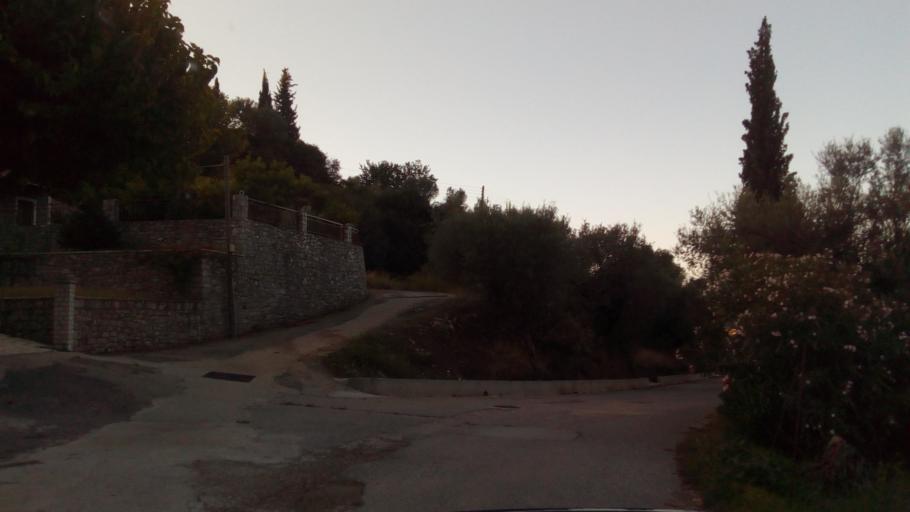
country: GR
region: West Greece
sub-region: Nomos Aitolias kai Akarnanias
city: Nafpaktos
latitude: 38.4058
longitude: 21.7977
